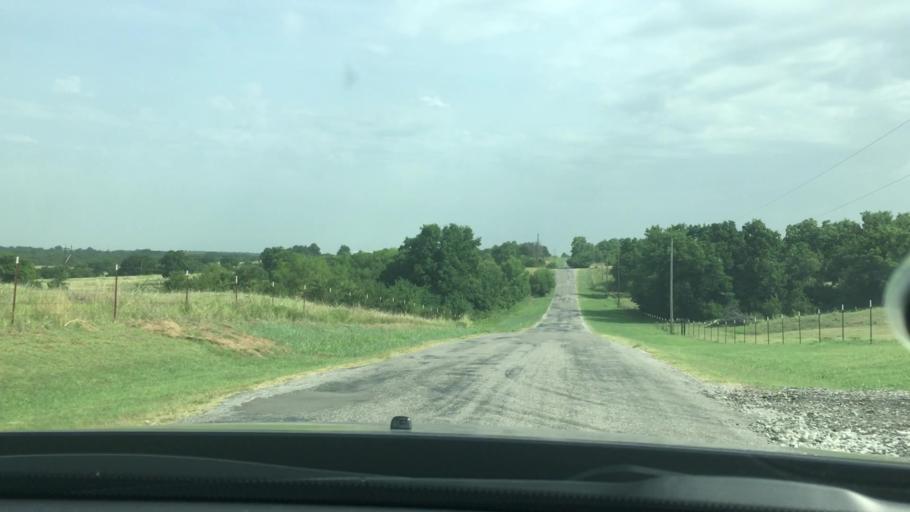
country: US
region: Oklahoma
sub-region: Garvin County
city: Pauls Valley
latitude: 34.8150
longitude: -97.1956
